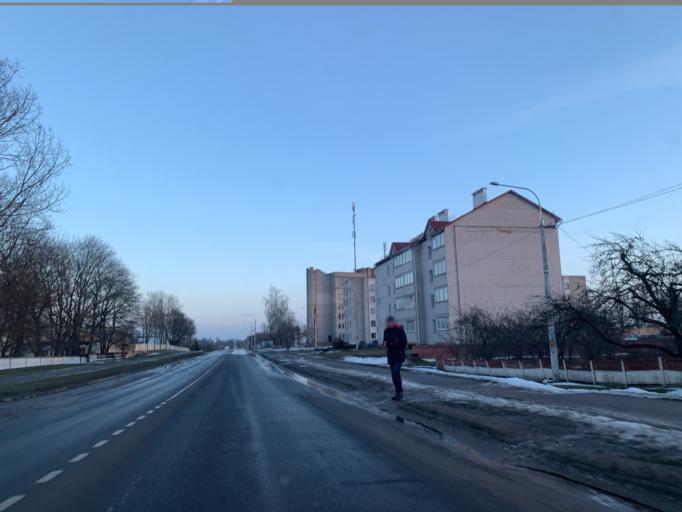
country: BY
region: Minsk
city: Nyasvizh
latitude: 53.2309
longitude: 26.6569
